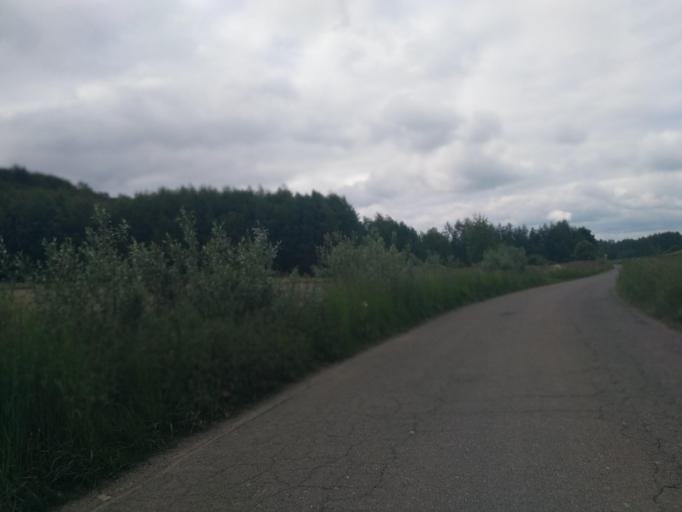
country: PL
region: Subcarpathian Voivodeship
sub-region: Powiat jasielski
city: Tarnowiec
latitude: 49.6900
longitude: 21.5833
